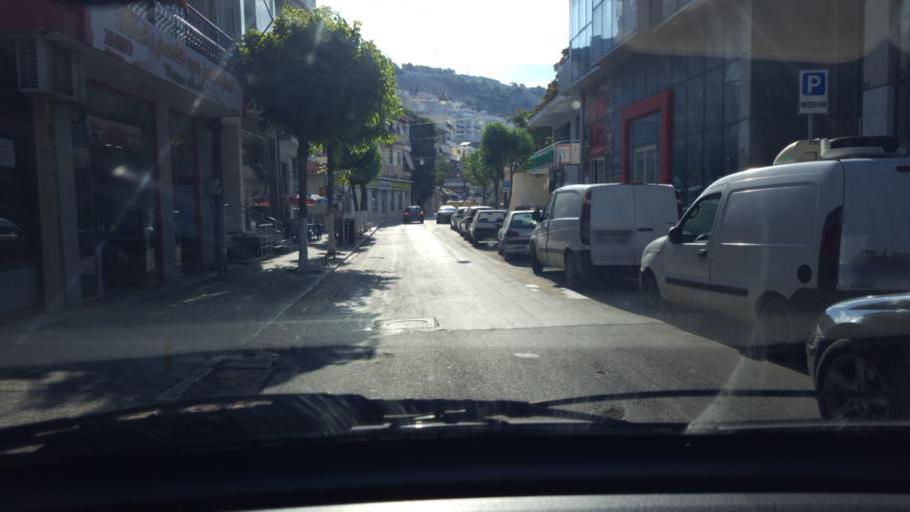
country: AL
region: Vlore
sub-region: Rrethi i Sarandes
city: Sarande
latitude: 39.8747
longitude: 20.0078
